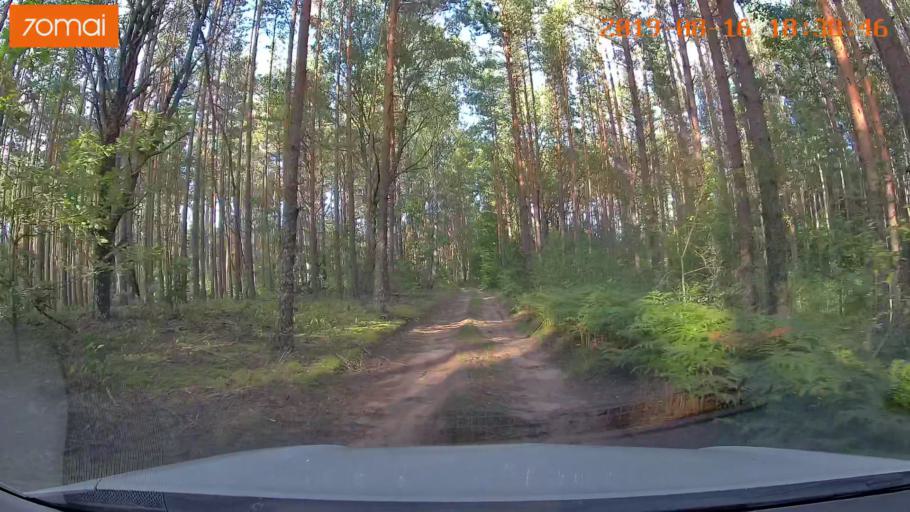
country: BY
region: Mogilev
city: Asipovichy
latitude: 53.2109
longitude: 28.6375
